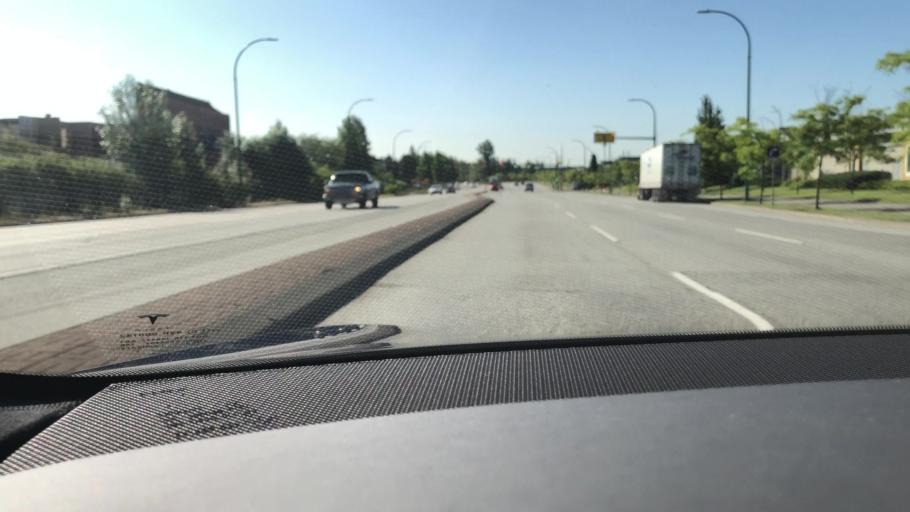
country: CA
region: British Columbia
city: New Westminster
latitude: 49.2012
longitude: -122.9810
